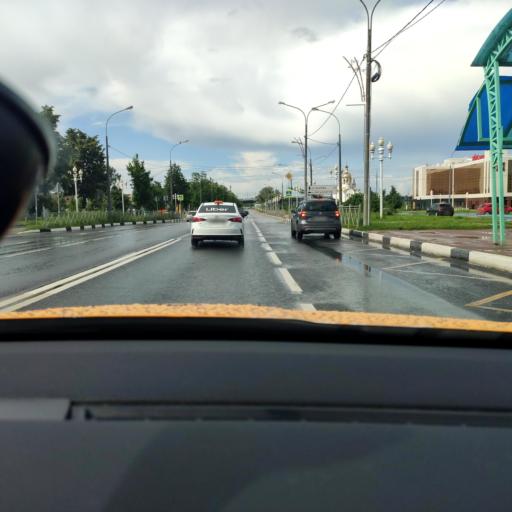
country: RU
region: Moskovskaya
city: Stupino
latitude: 54.8985
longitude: 38.0805
